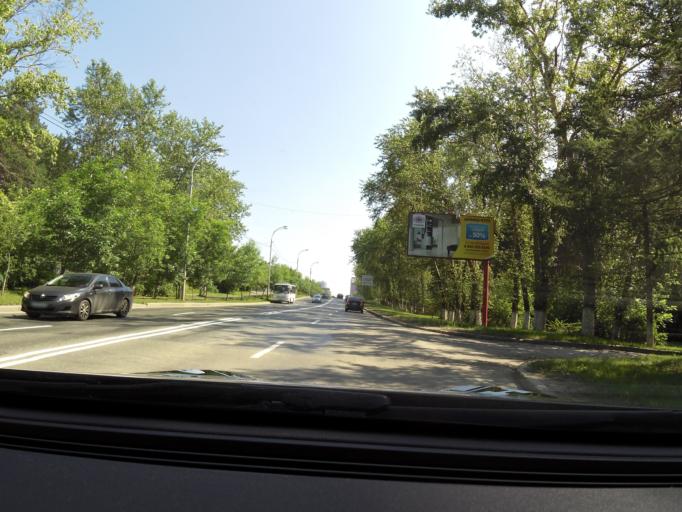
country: RU
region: Sverdlovsk
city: Shirokaya Rechka
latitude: 56.8161
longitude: 60.5273
